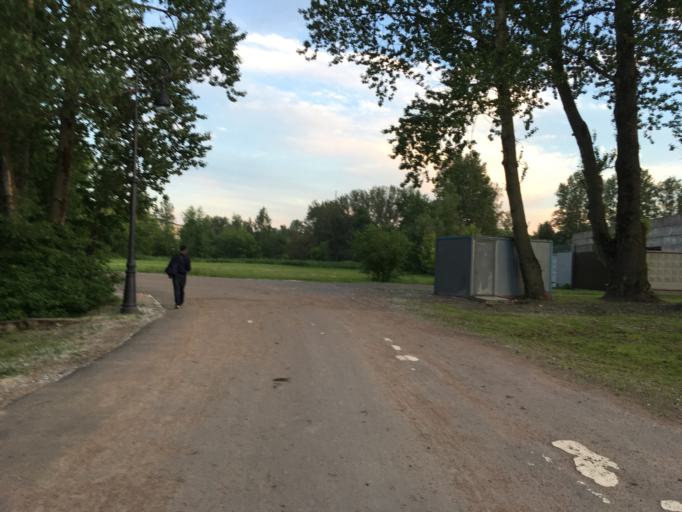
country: RU
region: St.-Petersburg
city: Admiralteisky
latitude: 59.9016
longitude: 30.2545
